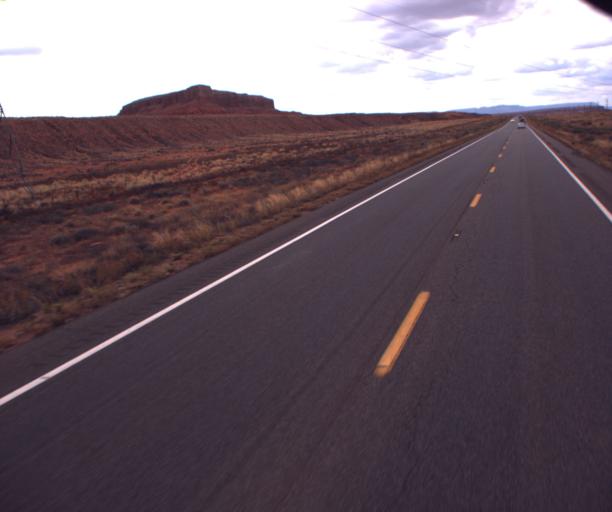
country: US
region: Arizona
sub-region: Navajo County
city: Kayenta
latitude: 36.8013
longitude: -109.9233
